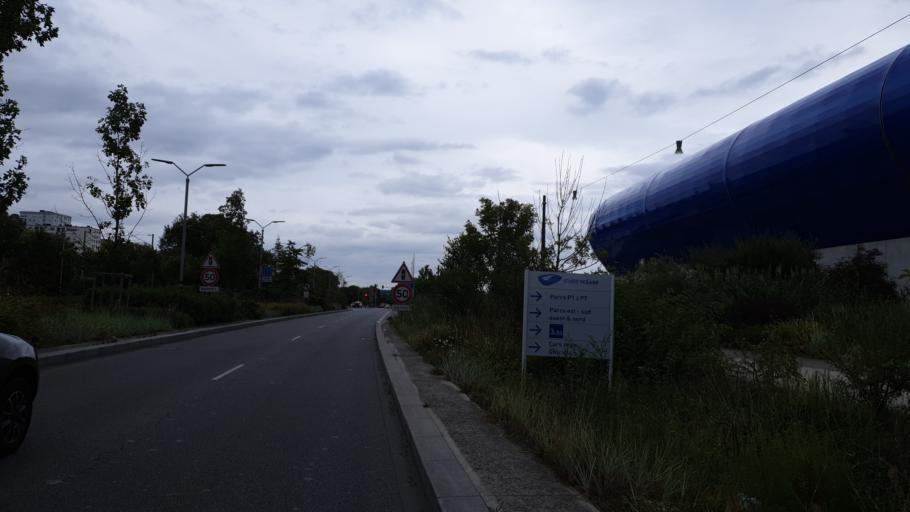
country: FR
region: Haute-Normandie
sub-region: Departement de la Seine-Maritime
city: Harfleur
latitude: 49.5000
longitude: 0.1686
